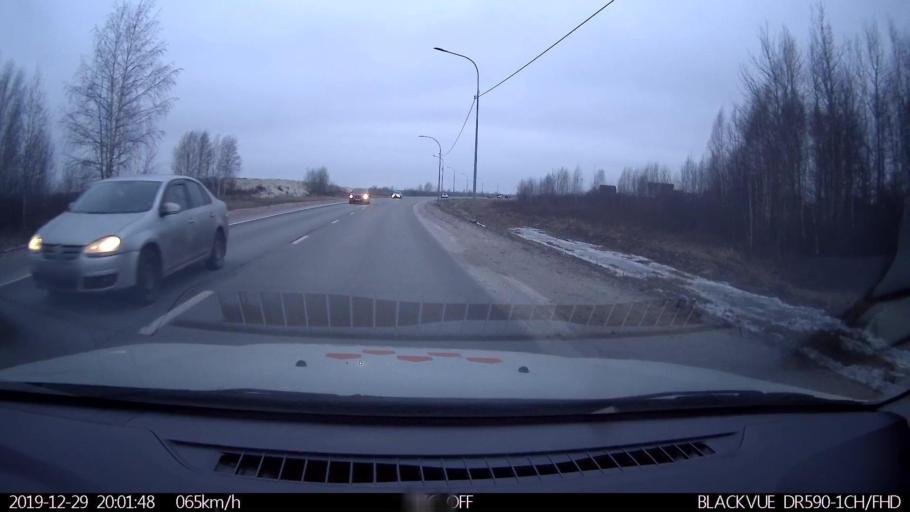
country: RU
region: Nizjnij Novgorod
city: Bor
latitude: 56.3606
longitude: 44.0380
